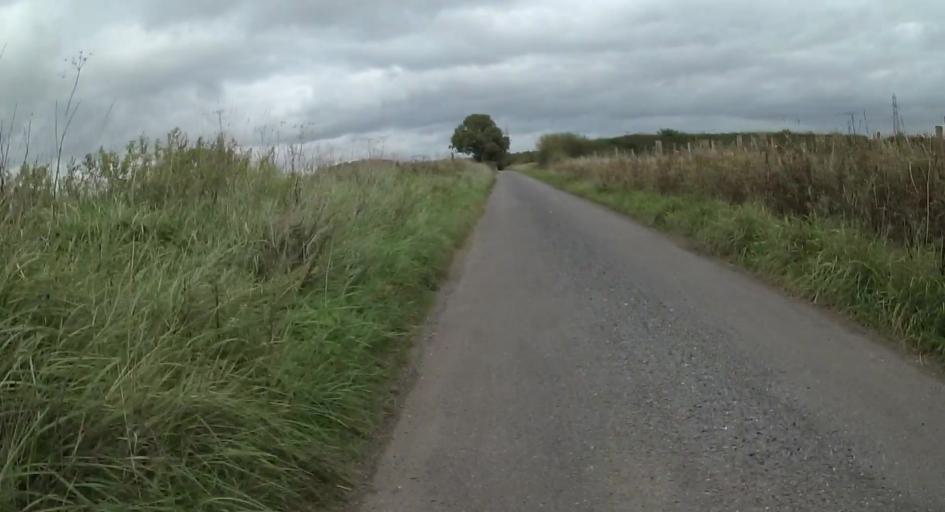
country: GB
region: England
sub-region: Hampshire
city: Alton
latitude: 51.1184
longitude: -0.9731
